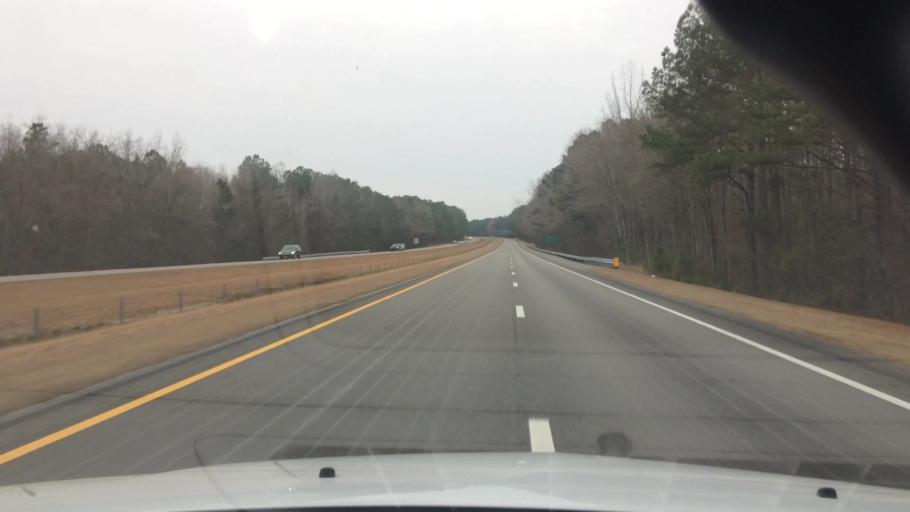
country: US
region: North Carolina
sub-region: Nash County
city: Spring Hope
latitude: 35.8889
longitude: -78.2026
